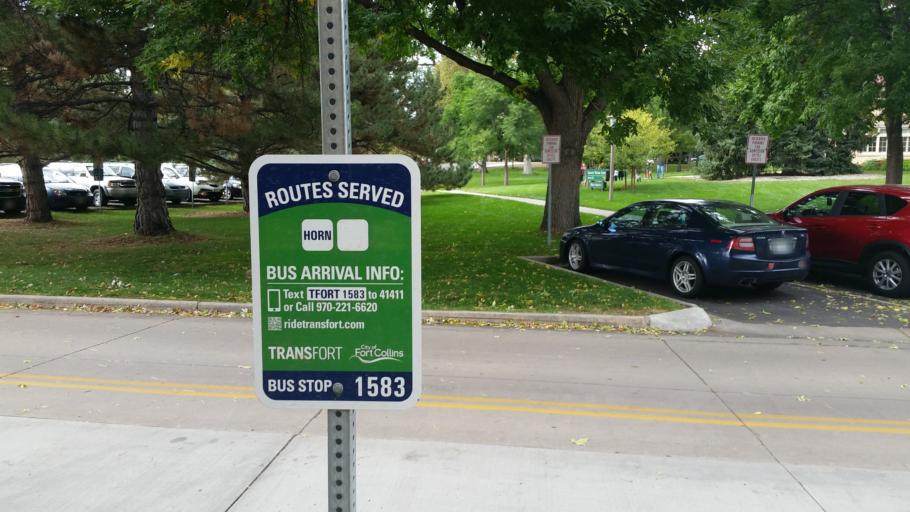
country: US
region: Colorado
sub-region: Larimer County
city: Fort Collins
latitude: 40.5770
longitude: -105.0820
